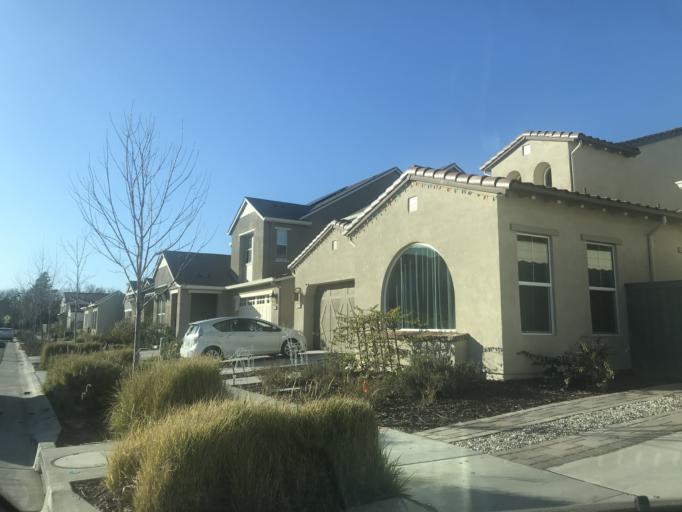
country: US
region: California
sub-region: Yolo County
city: Davis
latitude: 38.5669
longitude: -121.7426
